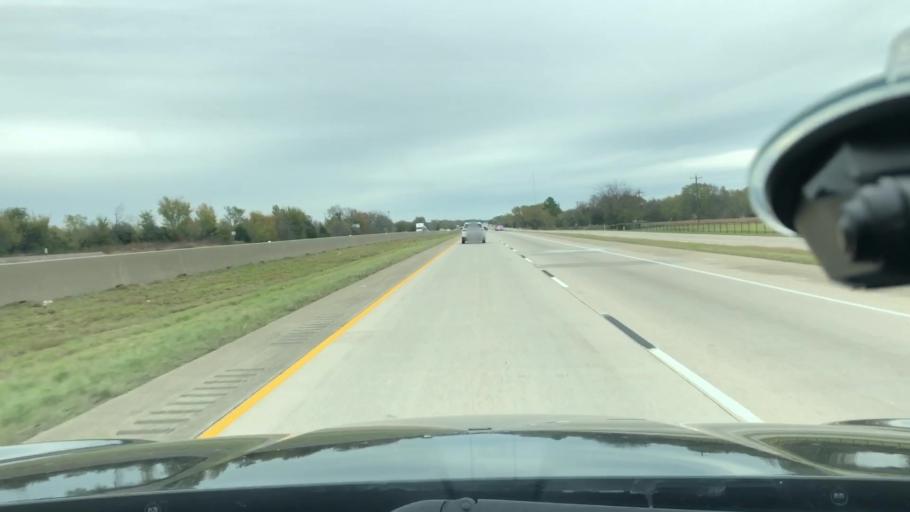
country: US
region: Texas
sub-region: Hopkins County
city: Sulphur Springs
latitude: 33.1289
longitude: -95.7642
